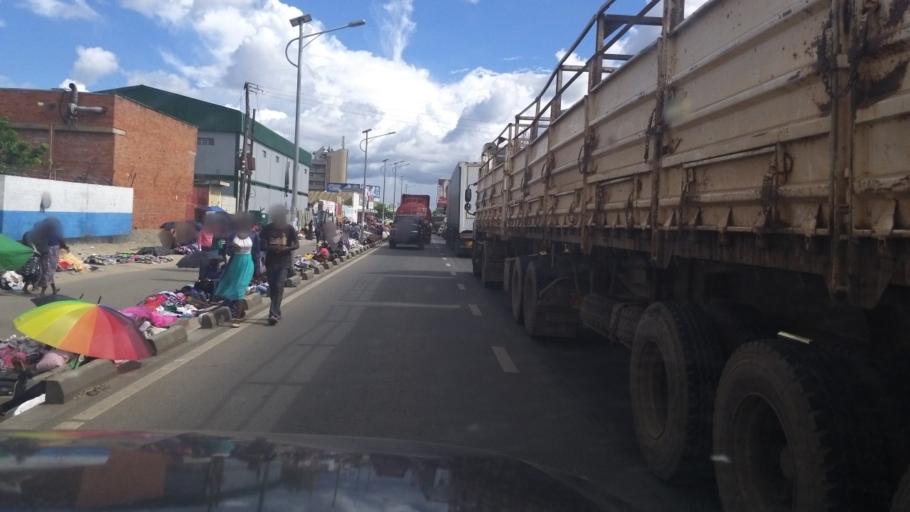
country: ZM
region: Lusaka
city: Lusaka
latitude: -15.4238
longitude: 28.2787
